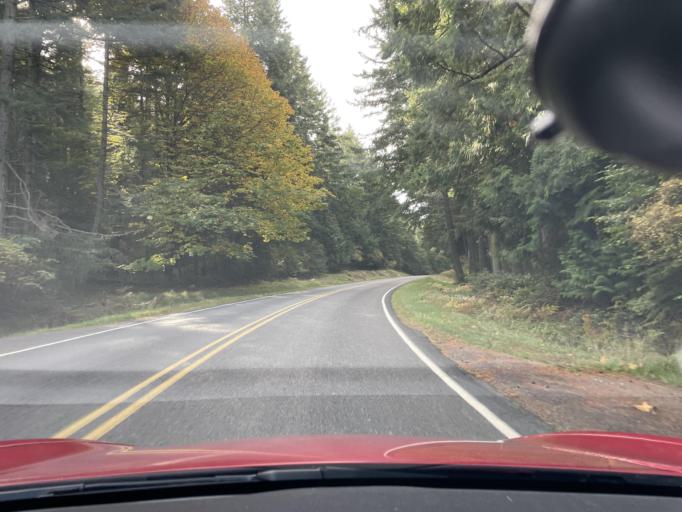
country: US
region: Washington
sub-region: San Juan County
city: Friday Harbor
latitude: 48.5908
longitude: -123.1384
